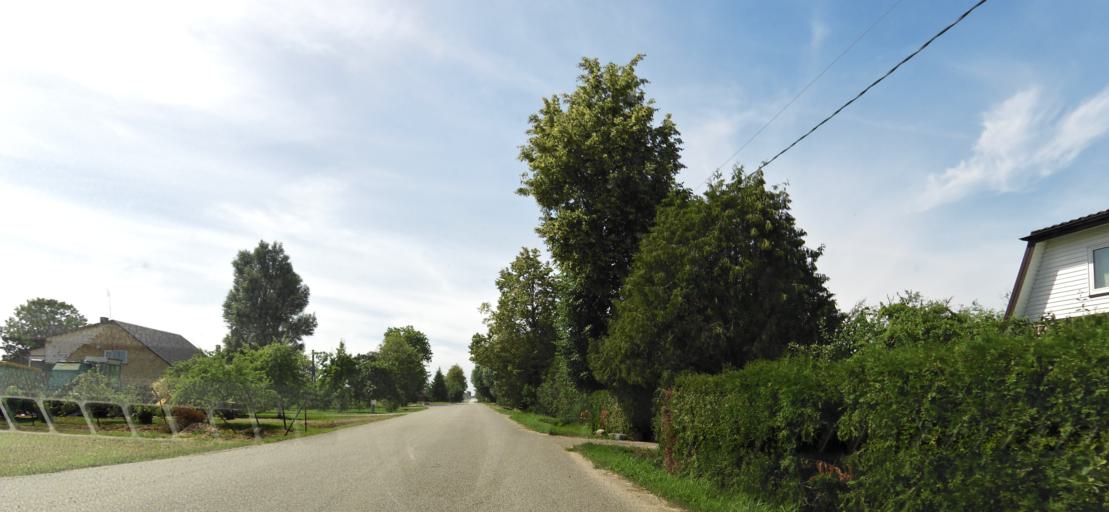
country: LT
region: Panevezys
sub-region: Panevezys City
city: Panevezys
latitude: 55.8825
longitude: 24.3036
